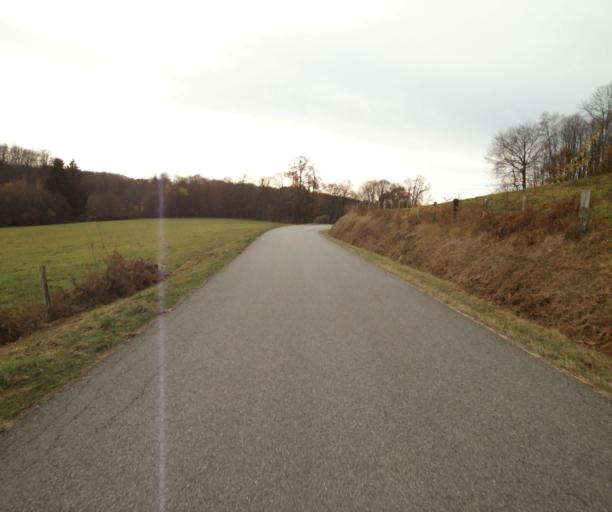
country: FR
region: Limousin
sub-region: Departement de la Correze
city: Sainte-Fortunade
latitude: 45.1821
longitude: 1.7562
